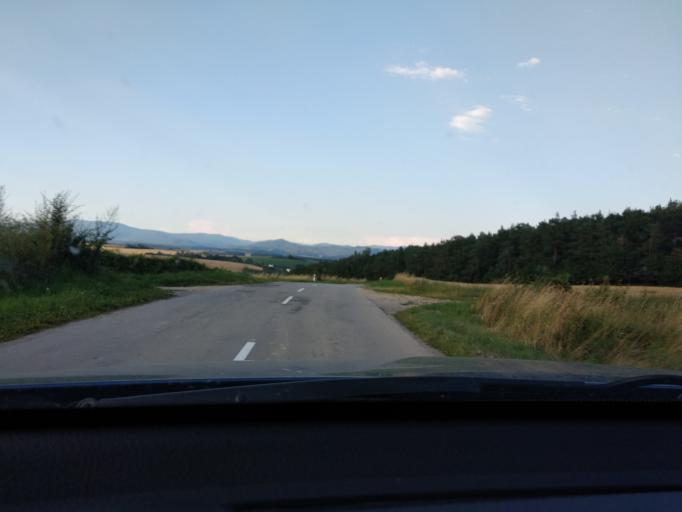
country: SK
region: Nitriansky
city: Banovce nad Bebravou
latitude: 48.7297
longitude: 18.1551
